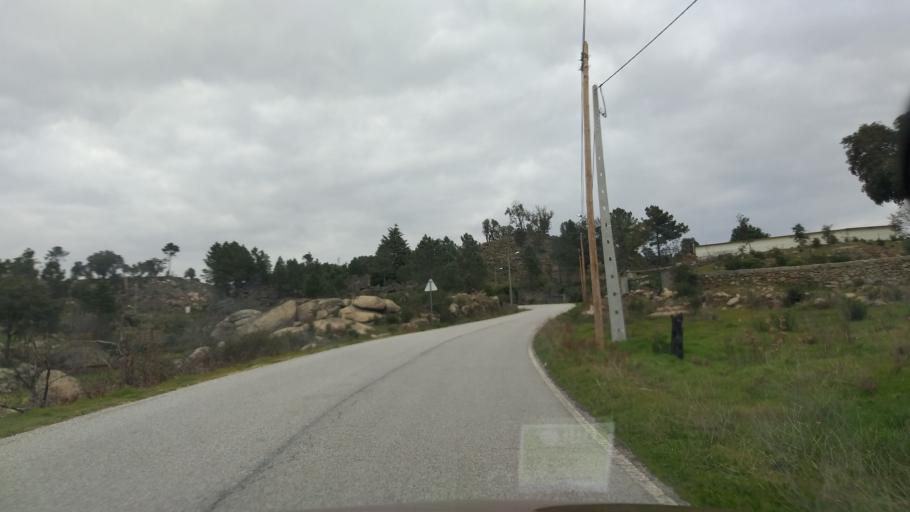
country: PT
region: Guarda
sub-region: Fornos de Algodres
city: Fornos de Algodres
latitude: 40.5728
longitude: -7.6060
